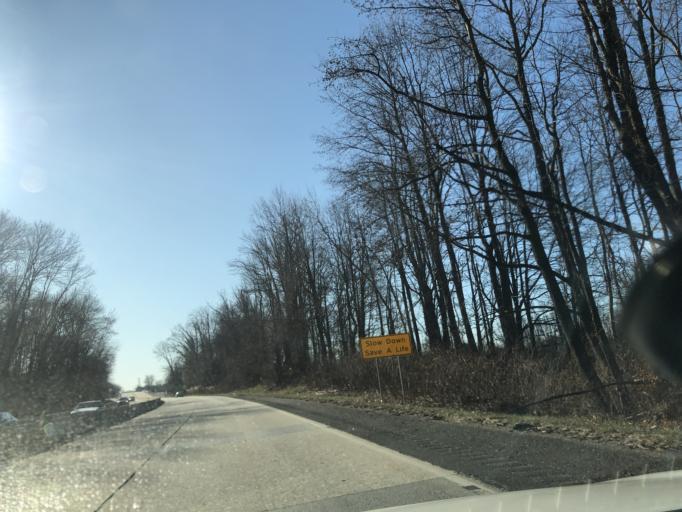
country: US
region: Pennsylvania
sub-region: Bucks County
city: Levittown
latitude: 40.1769
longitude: -74.8122
